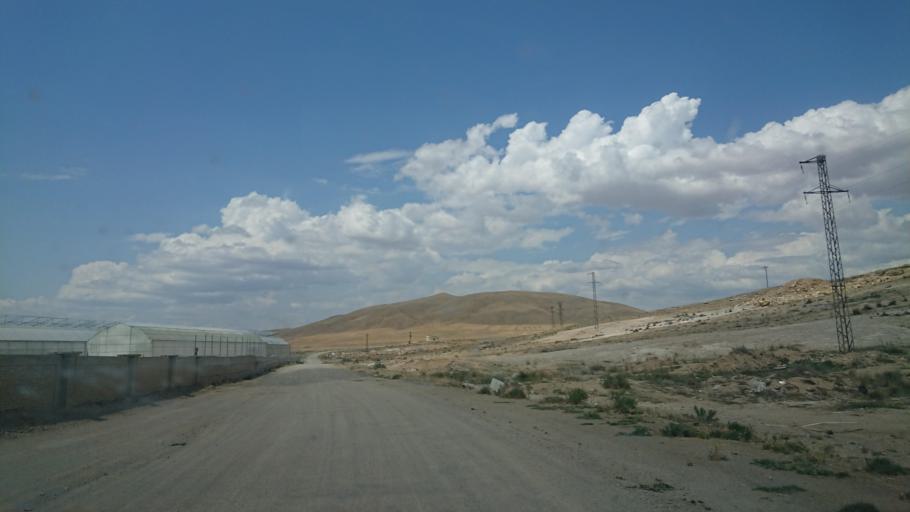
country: TR
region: Aksaray
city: Sariyahsi
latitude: 39.0008
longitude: 33.9117
